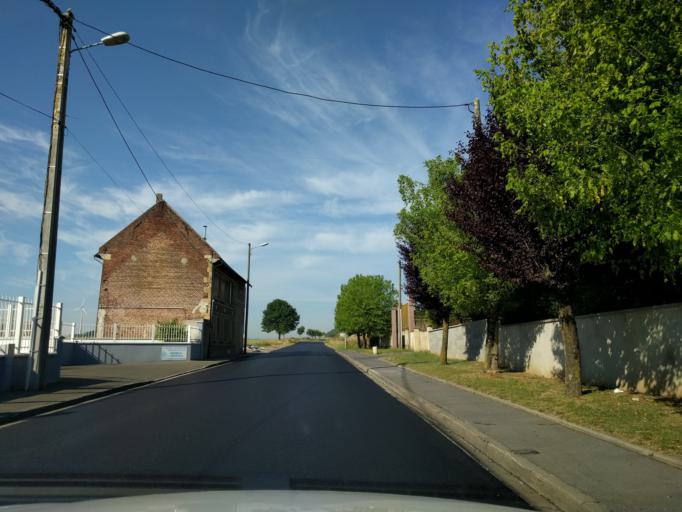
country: FR
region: Picardie
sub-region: Departement de l'Oise
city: Breteuil
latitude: 49.6025
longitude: 2.2842
